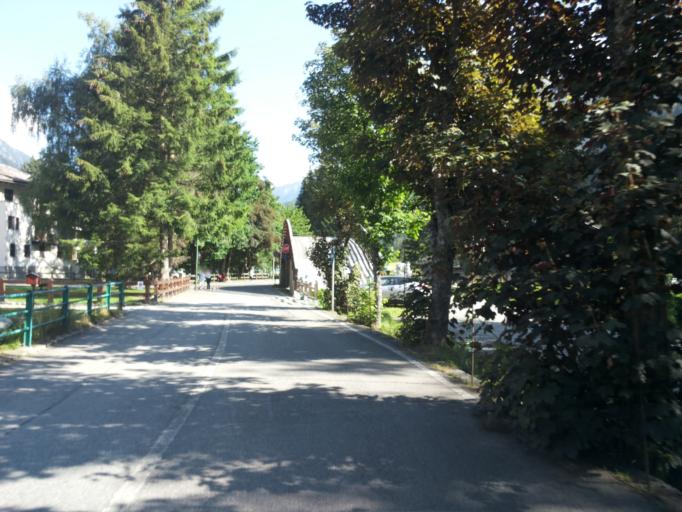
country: IT
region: Aosta Valley
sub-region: Valle d'Aosta
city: Gressoney-Saint-Jean
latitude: 45.7746
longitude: 7.8242
